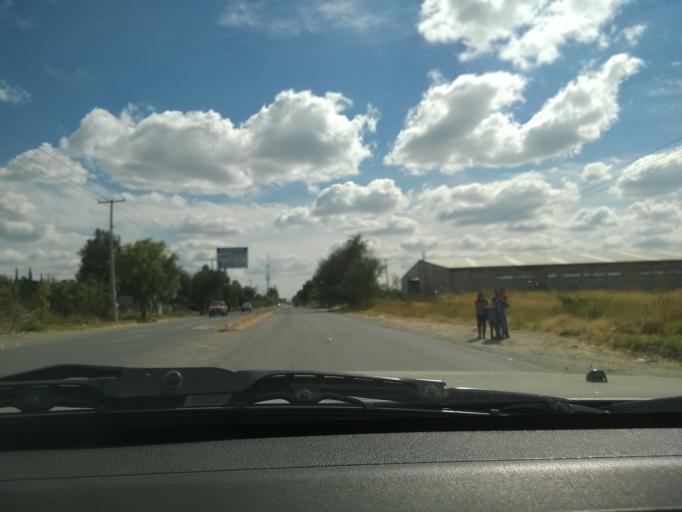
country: MX
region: Guanajuato
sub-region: Leon
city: El CERESO
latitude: 20.9845
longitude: -101.7020
